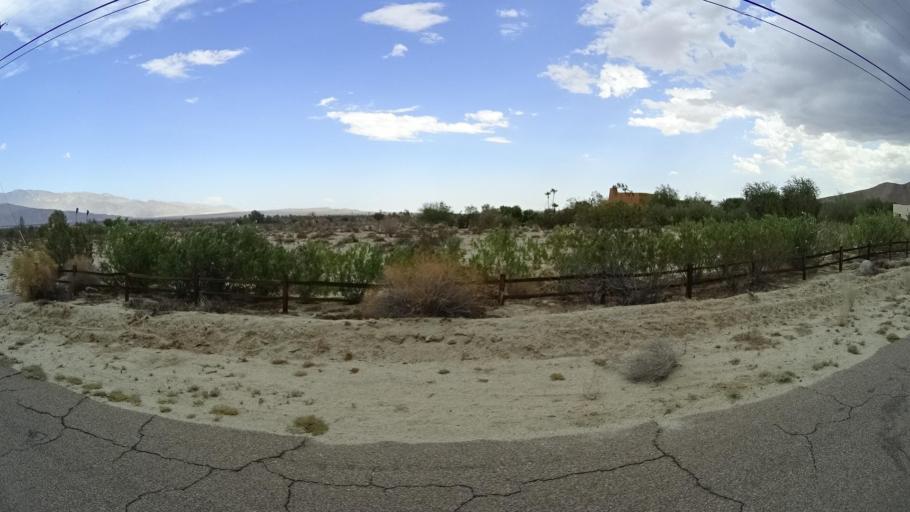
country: US
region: California
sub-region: San Diego County
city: Borrego Springs
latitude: 33.2604
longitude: -116.3911
